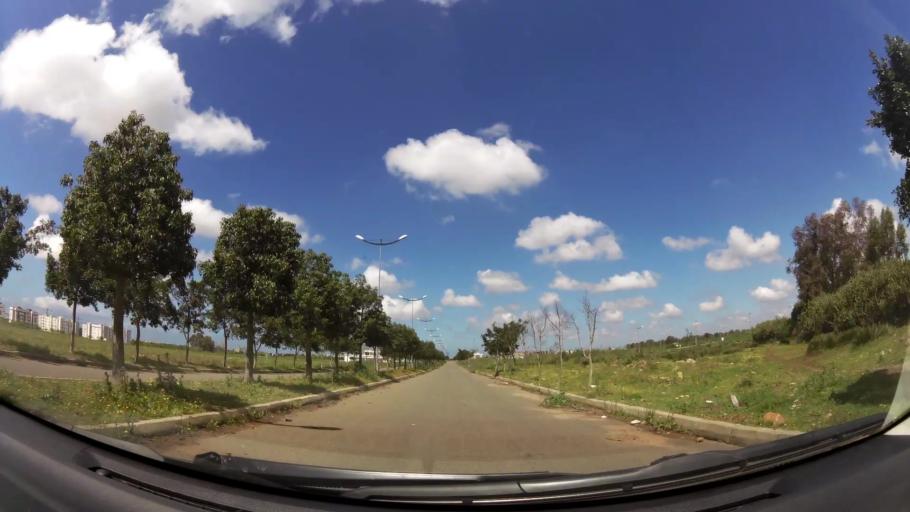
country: MA
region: Grand Casablanca
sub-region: Nouaceur
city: Dar Bouazza
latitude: 33.4148
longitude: -7.8288
